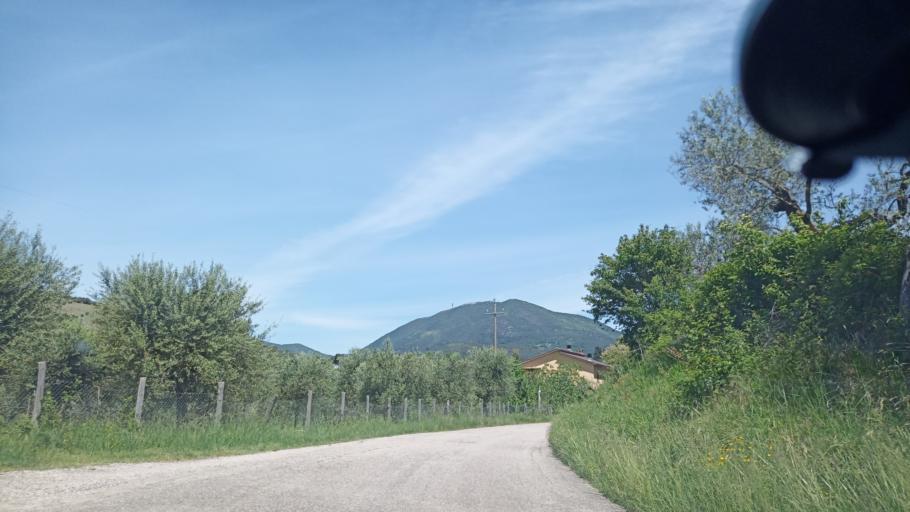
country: IT
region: Latium
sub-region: Provincia di Rieti
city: Torri in Sabina
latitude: 42.3563
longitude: 12.6346
